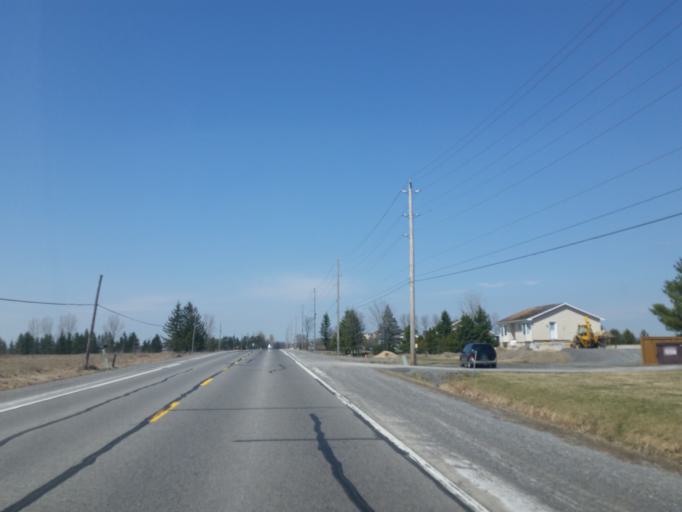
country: CA
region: Ontario
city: Bells Corners
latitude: 45.4471
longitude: -76.0551
